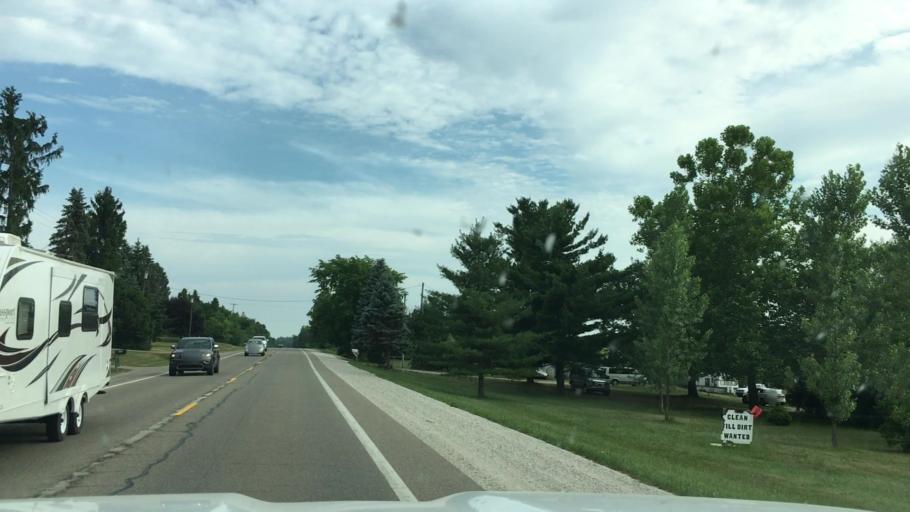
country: US
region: Michigan
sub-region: Sanilac County
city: Brown City
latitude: 43.1729
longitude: -83.0760
